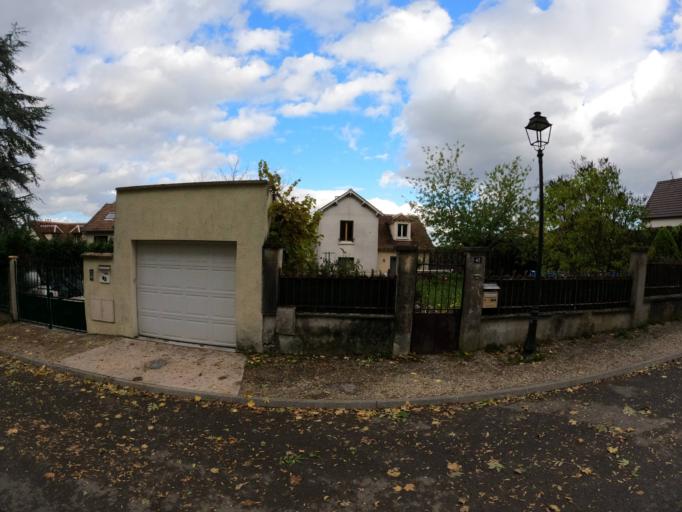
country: FR
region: Ile-de-France
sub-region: Departement de Seine-et-Marne
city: Coupvray
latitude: 48.8899
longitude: 2.7985
